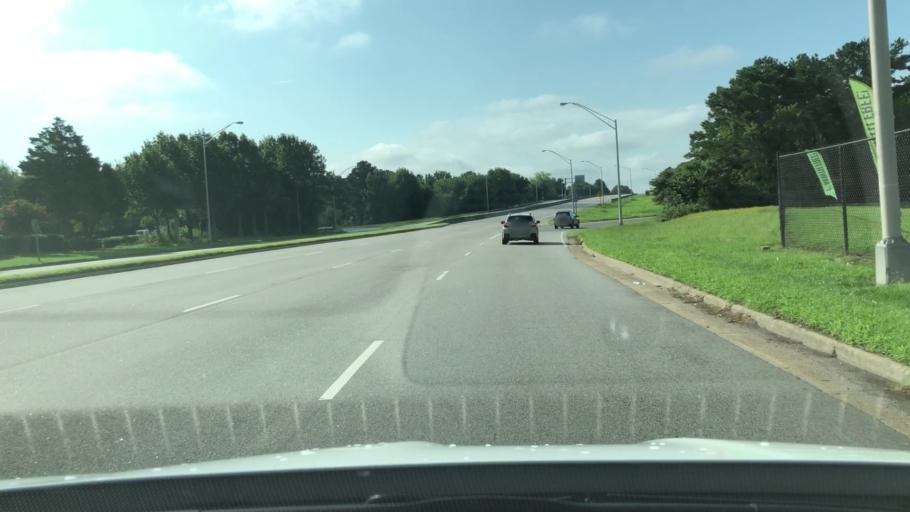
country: US
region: Virginia
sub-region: City of Chesapeake
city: Chesapeake
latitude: 36.7883
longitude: -76.2359
